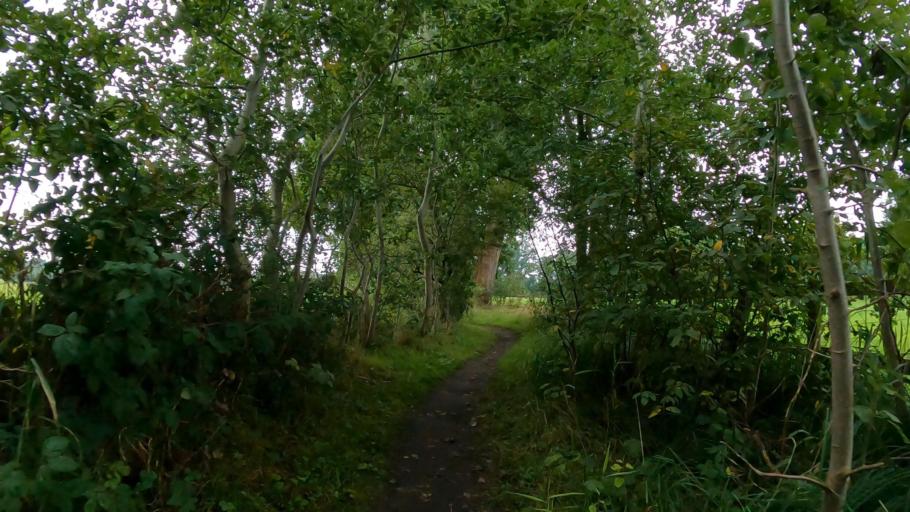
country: DE
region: Schleswig-Holstein
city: Rellingen
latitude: 53.6370
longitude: 9.8227
